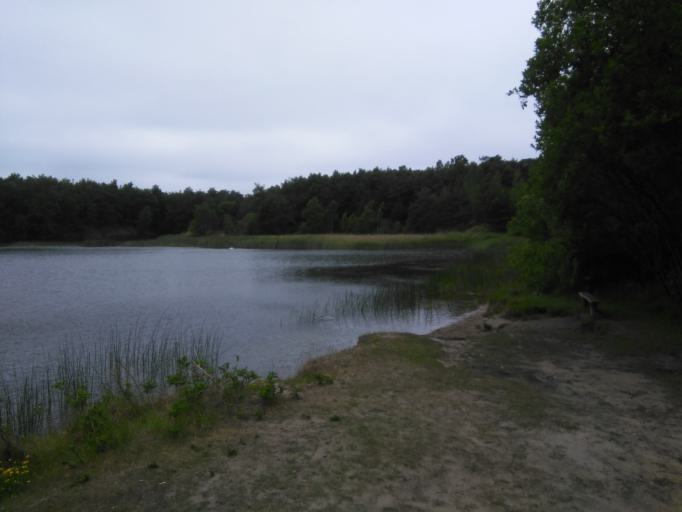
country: DK
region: Capital Region
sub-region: Bornholm Kommune
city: Ronne
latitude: 55.1467
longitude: 14.7118
